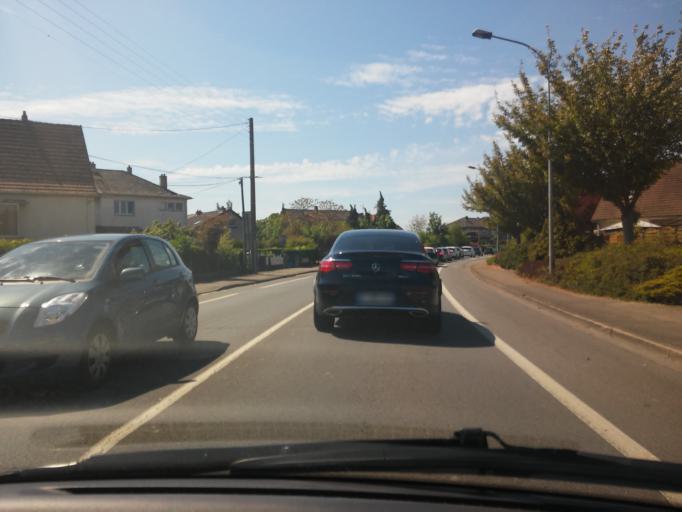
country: FR
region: Lorraine
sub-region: Departement de la Moselle
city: Hagondange
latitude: 49.2574
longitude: 6.1584
